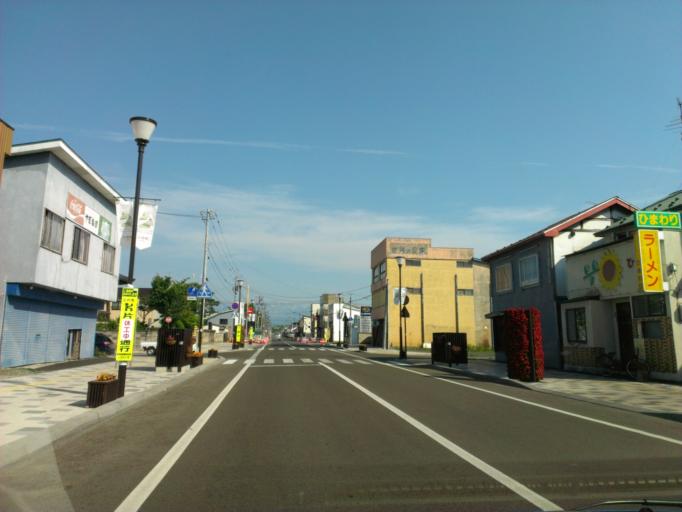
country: JP
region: Hokkaido
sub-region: Asahikawa-shi
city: Asahikawa
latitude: 43.5895
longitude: 142.4639
